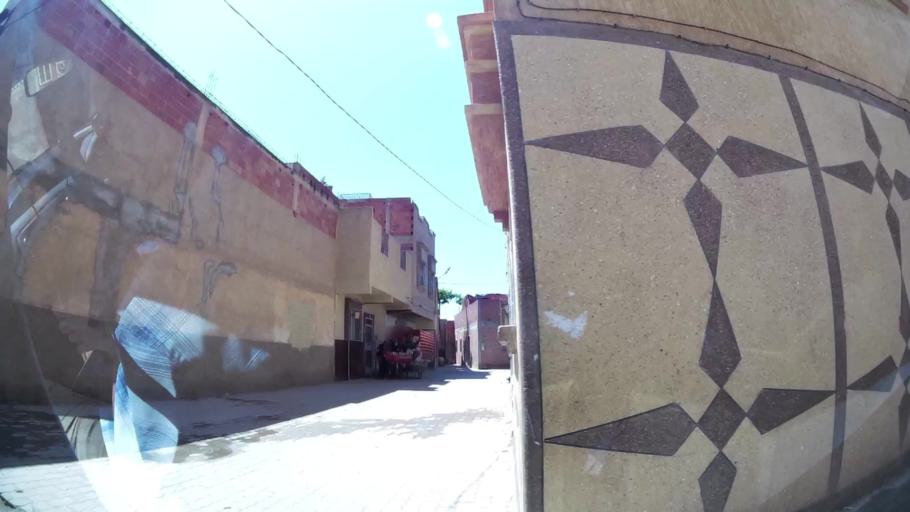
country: MA
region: Oriental
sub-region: Oujda-Angad
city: Oujda
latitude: 34.6922
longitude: -1.9413
